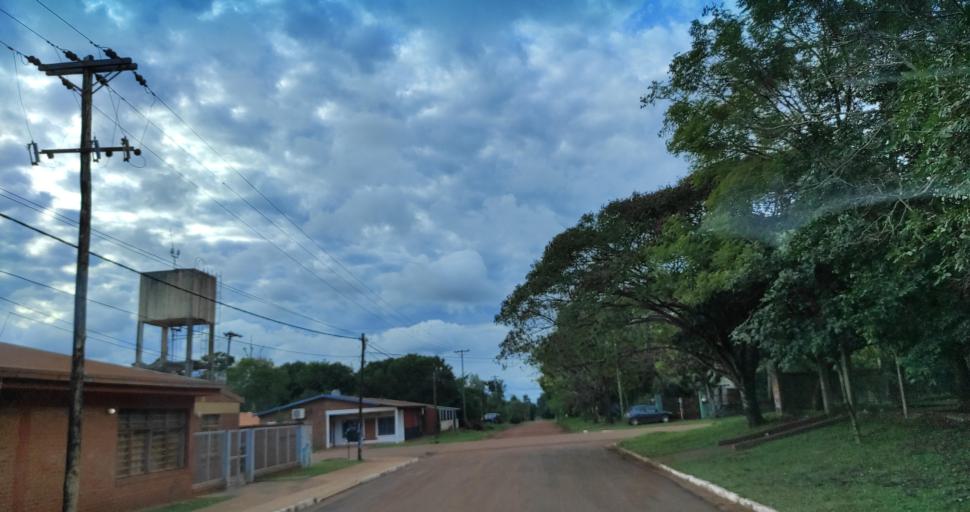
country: AR
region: Misiones
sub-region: Departamento de Candelaria
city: Candelaria
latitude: -27.4603
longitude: -55.7396
